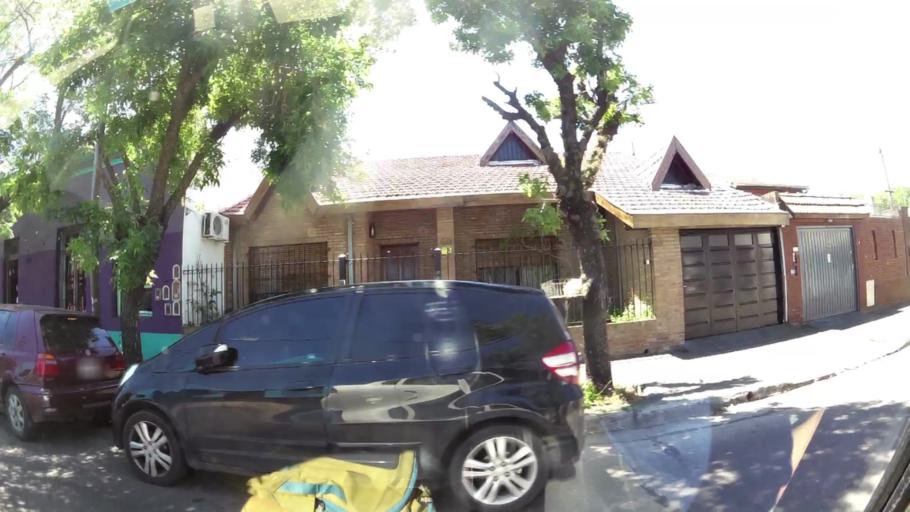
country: AR
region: Buenos Aires
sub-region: Partido de San Isidro
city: San Isidro
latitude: -34.4907
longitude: -58.5175
